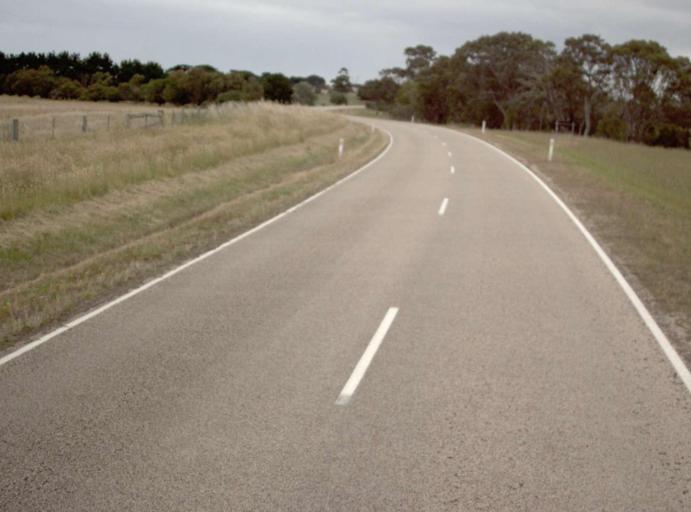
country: AU
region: Victoria
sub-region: East Gippsland
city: Bairnsdale
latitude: -37.9737
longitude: 147.4661
